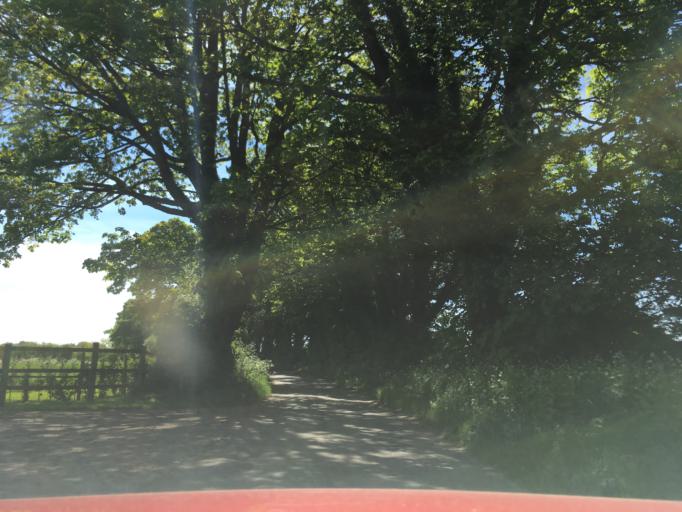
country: GB
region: England
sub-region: Gloucestershire
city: Stroud
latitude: 51.7408
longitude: -2.1817
